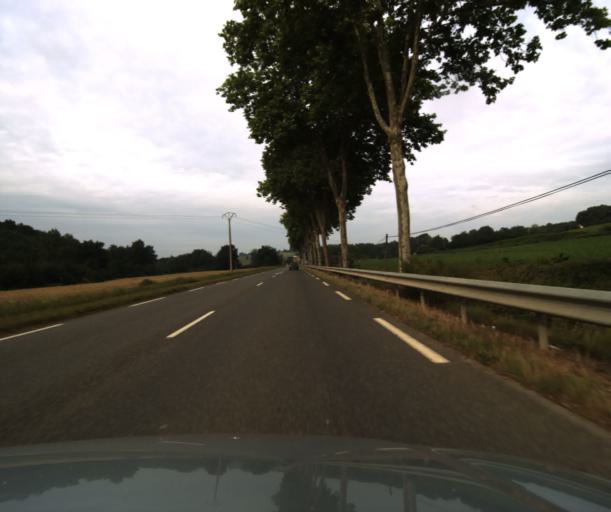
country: FR
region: Midi-Pyrenees
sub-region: Departement du Gers
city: Mirande
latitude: 43.4887
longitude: 0.3570
